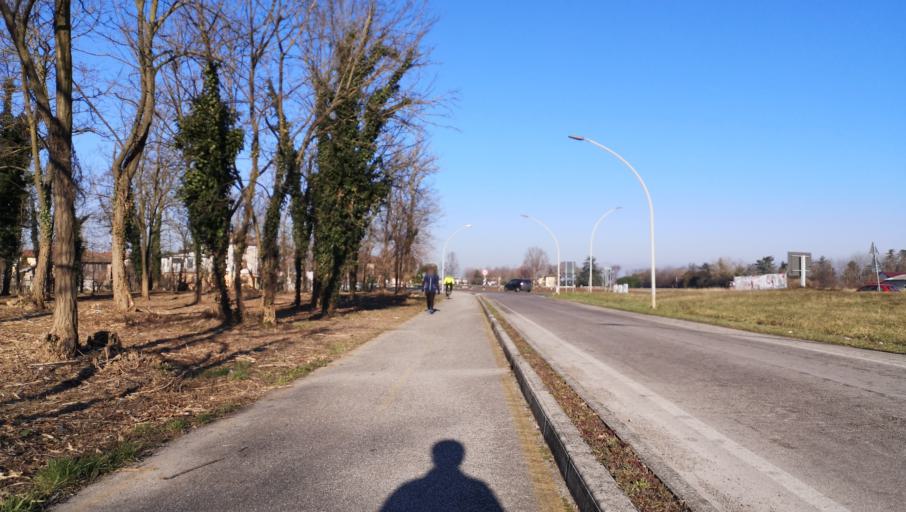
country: IT
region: Friuli Venezia Giulia
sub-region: Provincia di Udine
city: Palmanova
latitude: 45.9086
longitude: 13.3018
